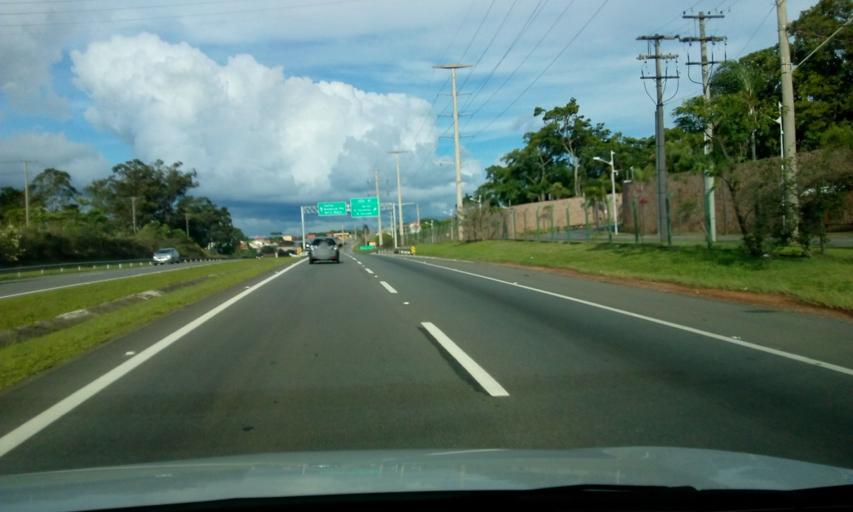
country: BR
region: Sao Paulo
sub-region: Jundiai
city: Jundiai
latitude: -23.1547
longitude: -46.8832
